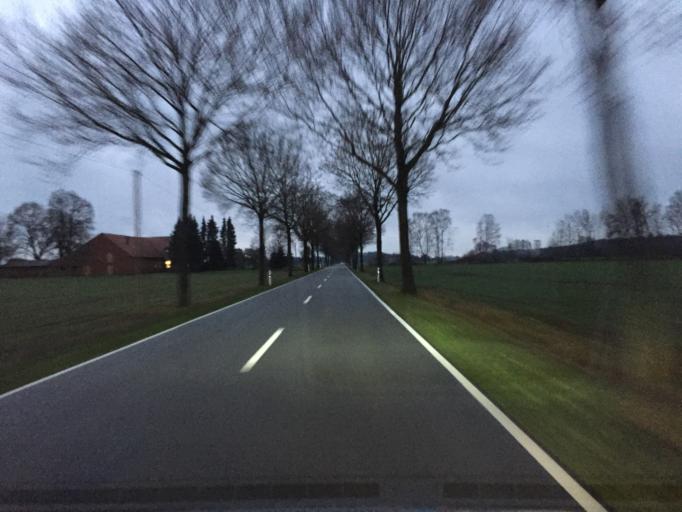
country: DE
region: Lower Saxony
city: Schwaforden
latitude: 52.7660
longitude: 8.8317
